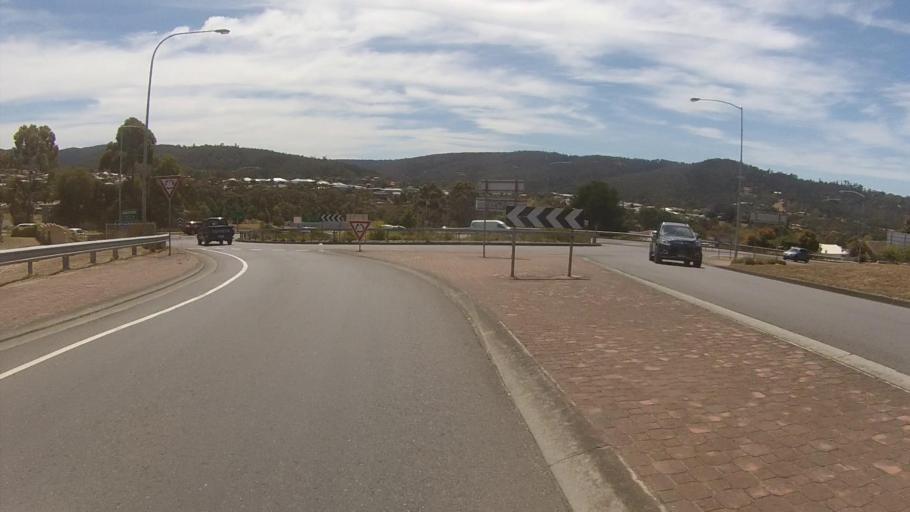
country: AU
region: Tasmania
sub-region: Kingborough
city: Kingston
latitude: -42.9761
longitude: 147.3039
